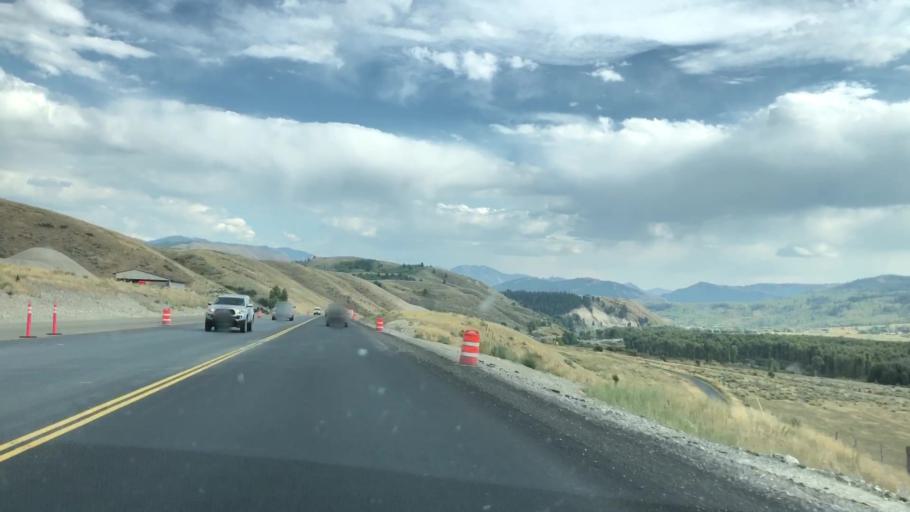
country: US
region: Wyoming
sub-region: Teton County
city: South Park
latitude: 43.4028
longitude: -110.7560
